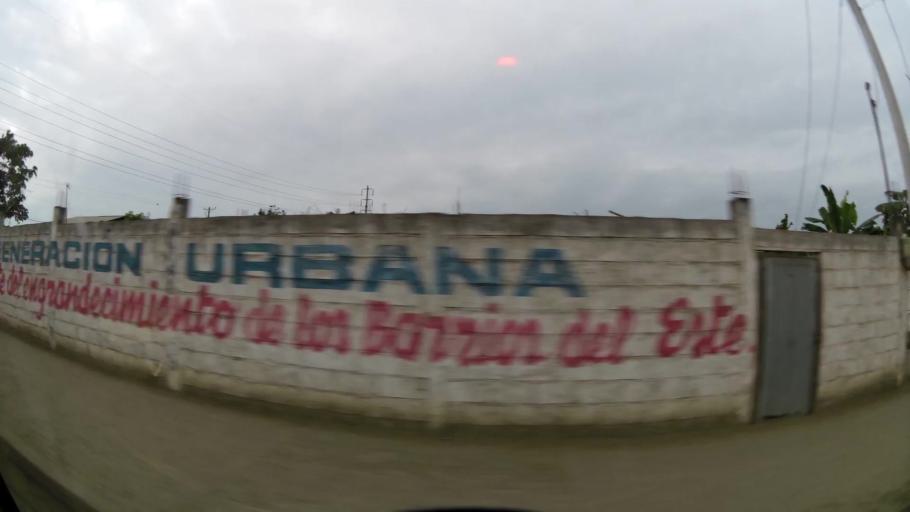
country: EC
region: El Oro
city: Machala
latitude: -3.2681
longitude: -79.9255
